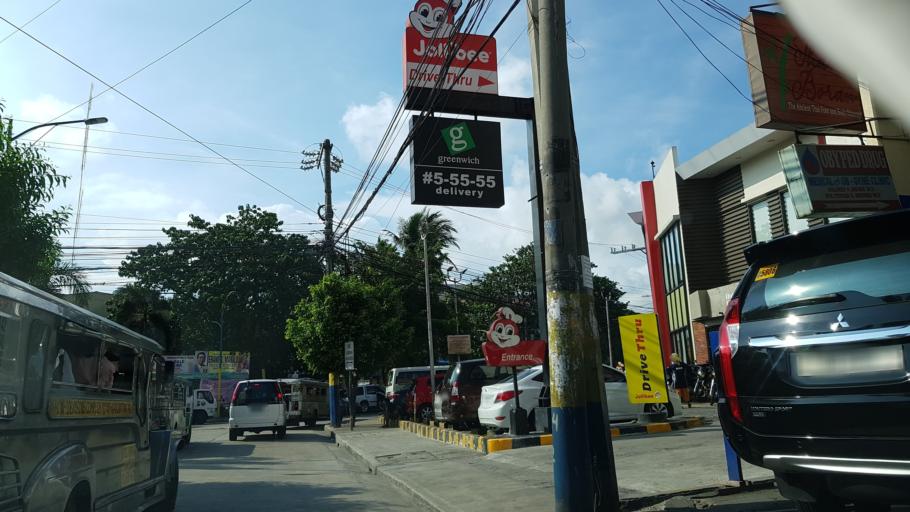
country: PH
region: Metro Manila
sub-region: Mandaluyong
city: Mandaluyong City
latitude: 14.5765
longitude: 121.0351
